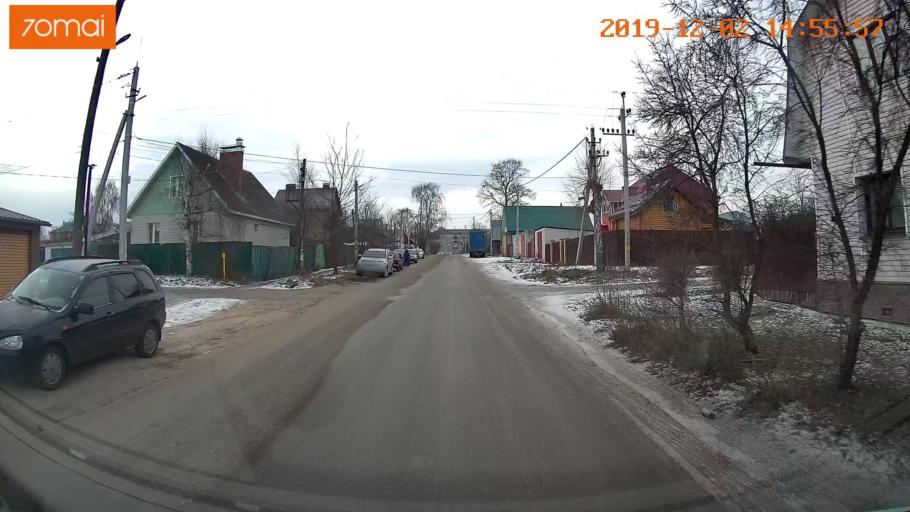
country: RU
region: Ivanovo
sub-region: Gorod Ivanovo
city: Ivanovo
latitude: 56.9723
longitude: 41.0181
